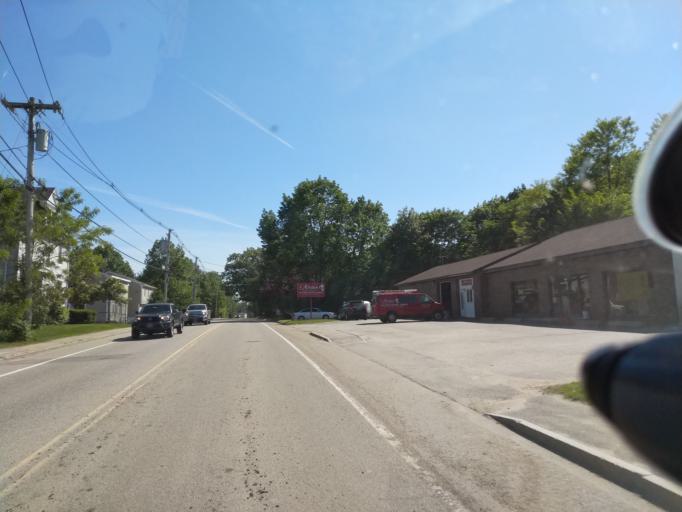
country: US
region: Maine
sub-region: Cumberland County
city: Westbrook
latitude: 43.7061
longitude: -70.3189
